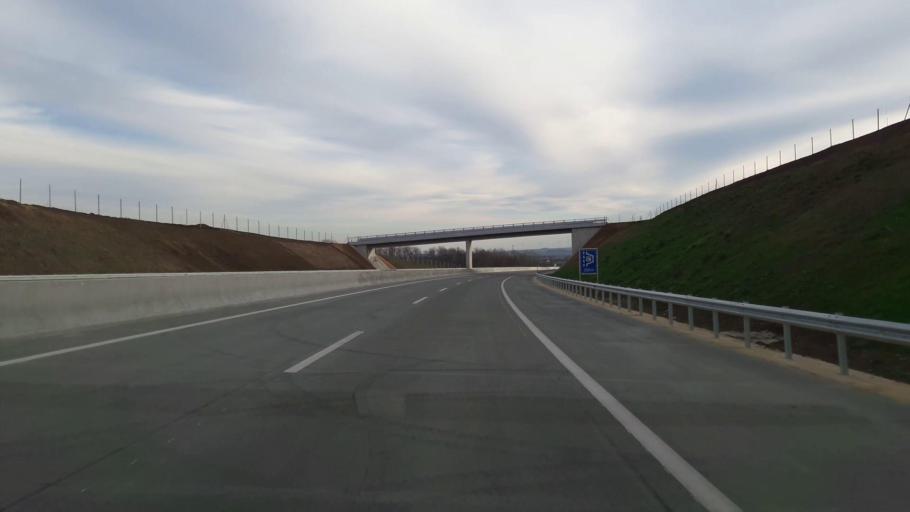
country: AT
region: Lower Austria
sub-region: Politischer Bezirk Mistelbach
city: Herrnbaumgarten
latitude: 48.6737
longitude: 16.6729
